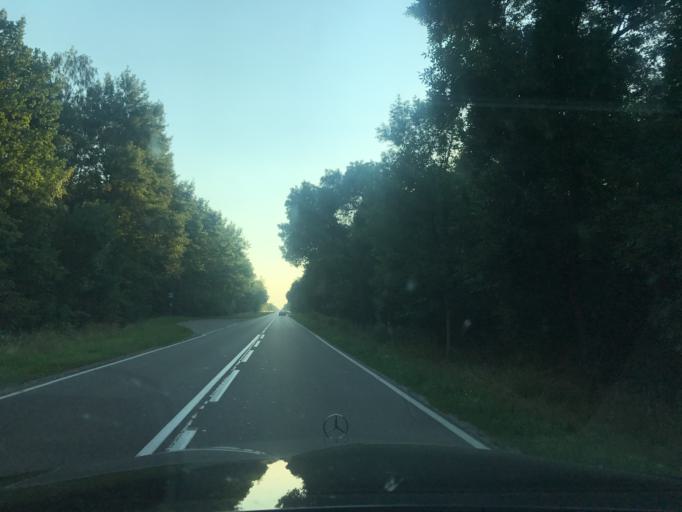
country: PL
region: Lublin Voivodeship
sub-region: Powiat parczewski
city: Debowa Kloda
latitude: 51.6452
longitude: 22.9687
